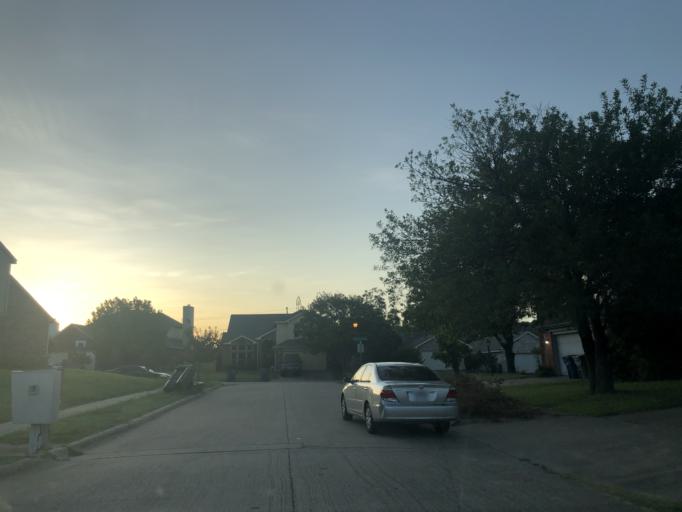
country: US
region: Texas
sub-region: Dallas County
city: Duncanville
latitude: 32.6571
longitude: -96.9643
